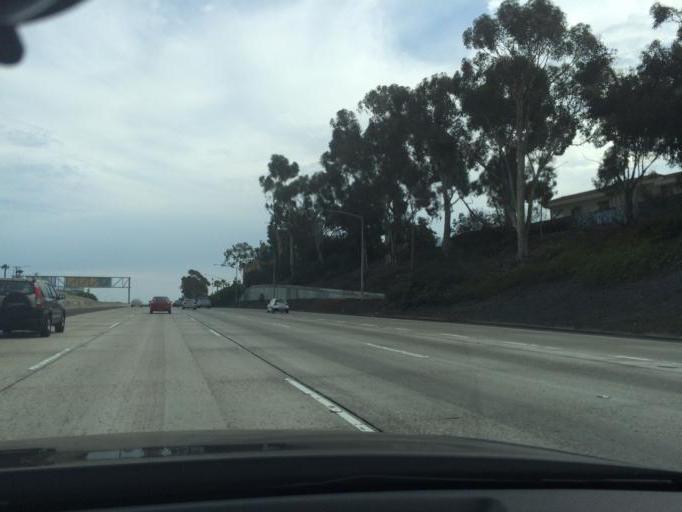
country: US
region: California
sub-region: San Diego County
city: San Diego
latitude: 32.8072
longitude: -117.1535
